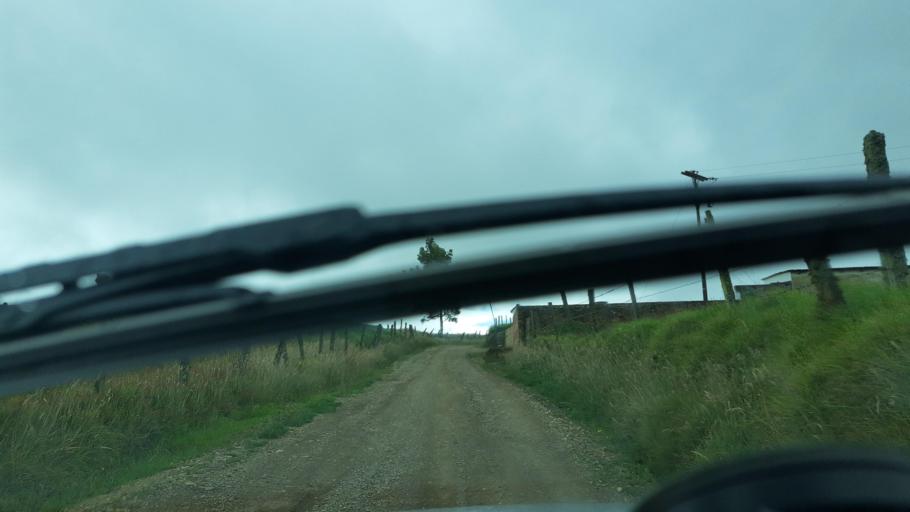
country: CO
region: Boyaca
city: Cucaita
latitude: 5.5068
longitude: -73.4405
